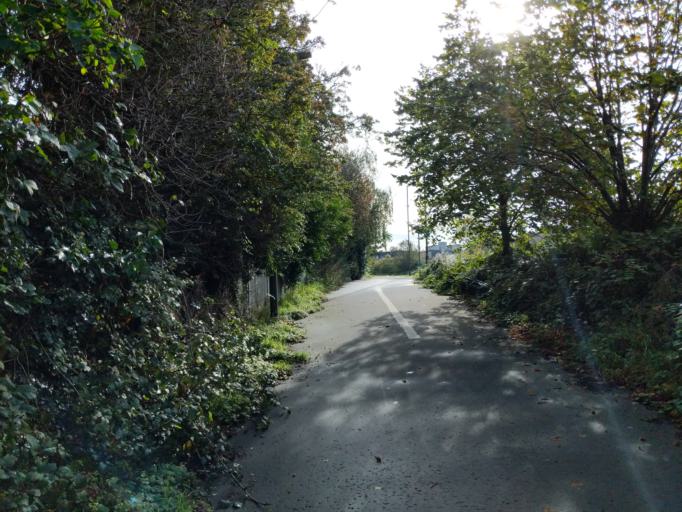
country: GB
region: Scotland
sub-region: Edinburgh
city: Edinburgh
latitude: 55.9763
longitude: -3.2411
